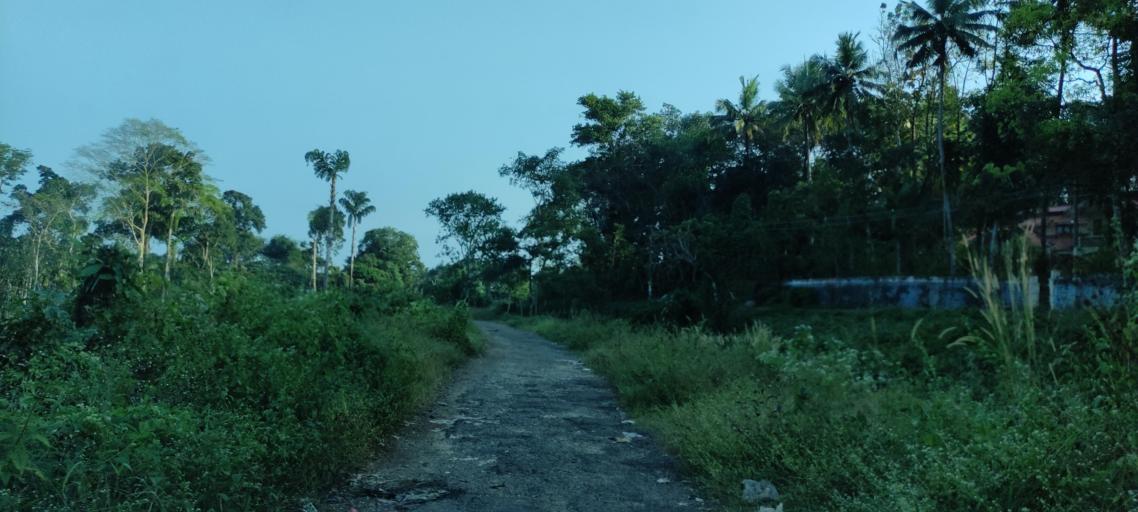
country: IN
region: Kerala
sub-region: Pattanamtitta
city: Adur
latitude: 9.1371
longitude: 76.7326
